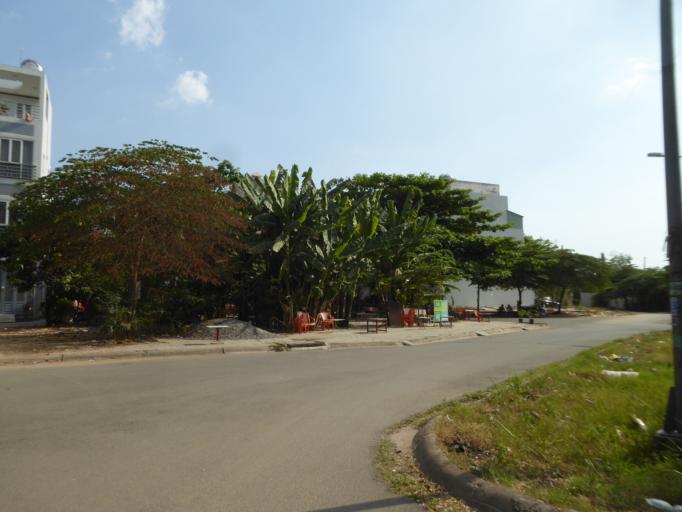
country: VN
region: Ho Chi Minh City
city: Quan Sau
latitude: 10.7395
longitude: 106.6185
